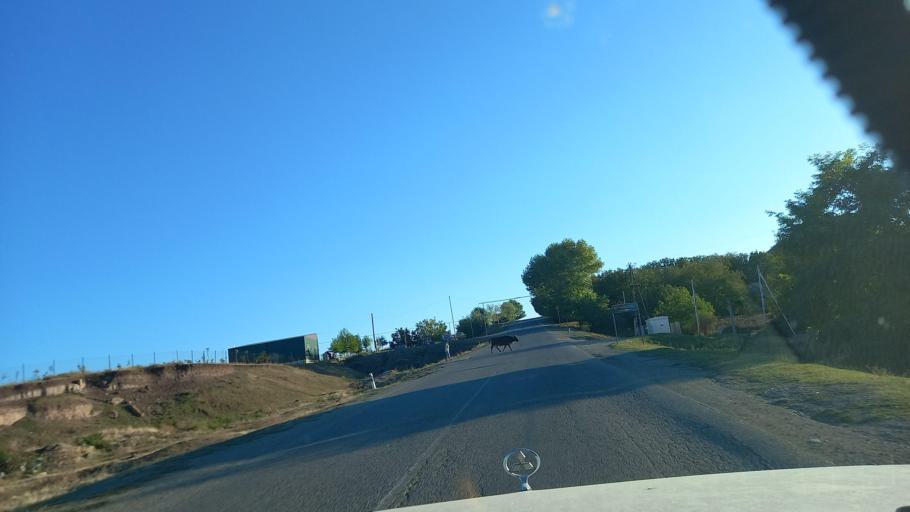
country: AZ
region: Shamkir Rayon
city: Shamkhor
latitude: 40.7732
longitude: 45.9589
